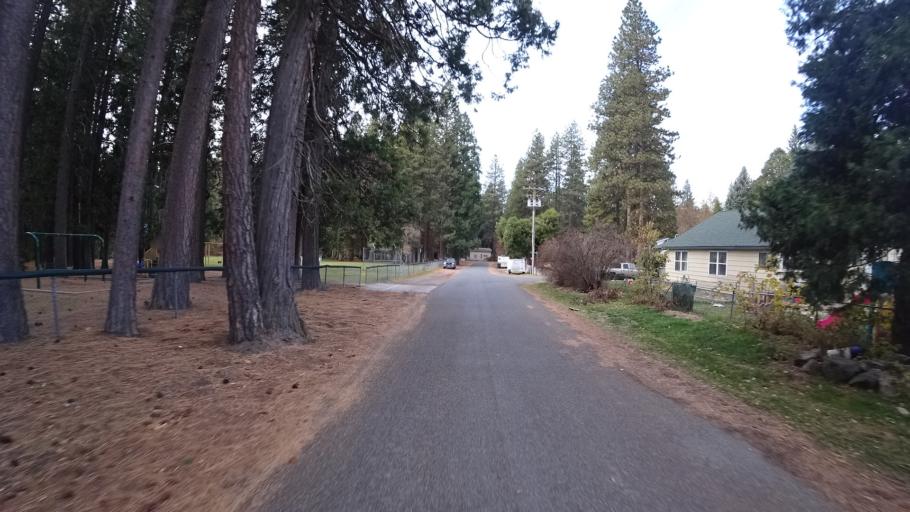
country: US
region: California
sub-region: Siskiyou County
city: Weed
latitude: 41.4450
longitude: -122.3631
